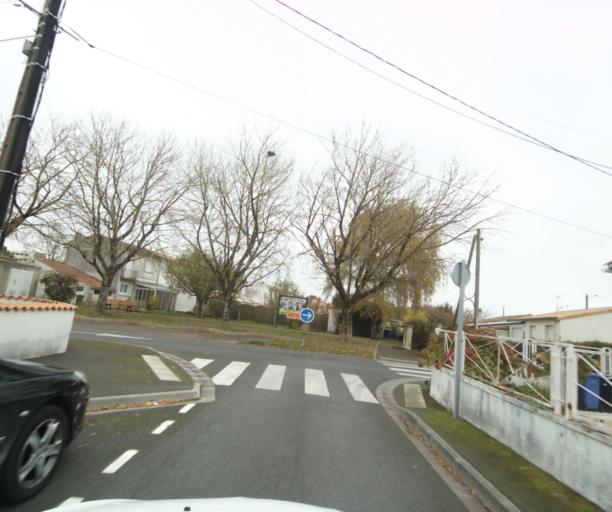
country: FR
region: Poitou-Charentes
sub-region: Departement de la Charente-Maritime
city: Les Gonds
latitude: 45.7346
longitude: -0.6191
